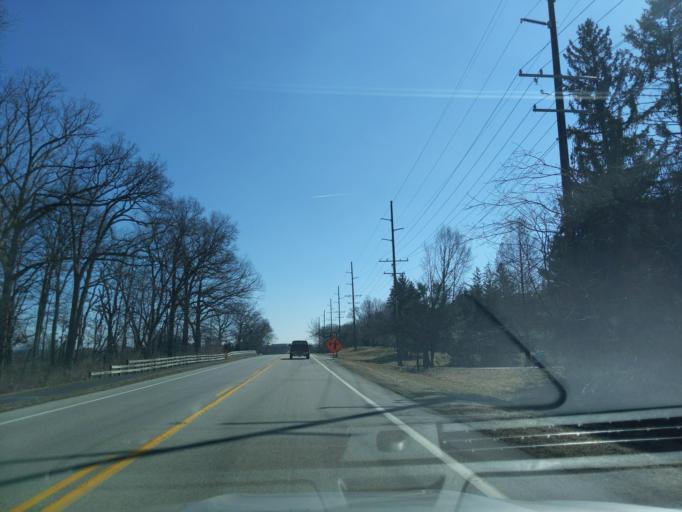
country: US
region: Indiana
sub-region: Tippecanoe County
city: West Lafayette
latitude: 40.4338
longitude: -86.9344
